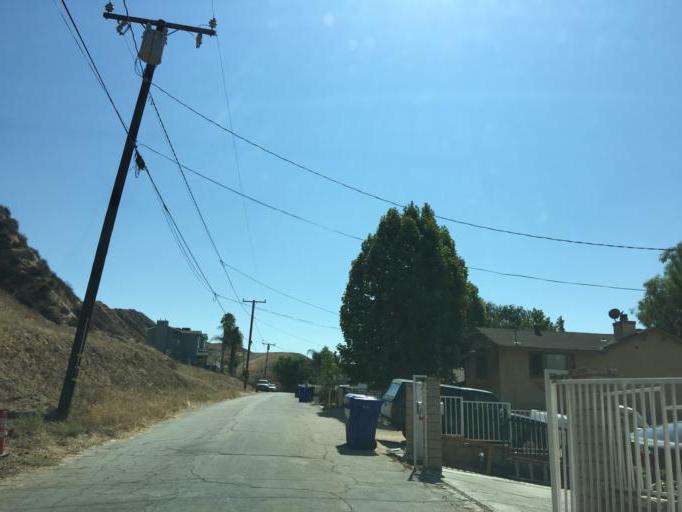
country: US
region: California
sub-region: Los Angeles County
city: Val Verde
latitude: 34.4480
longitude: -118.6538
